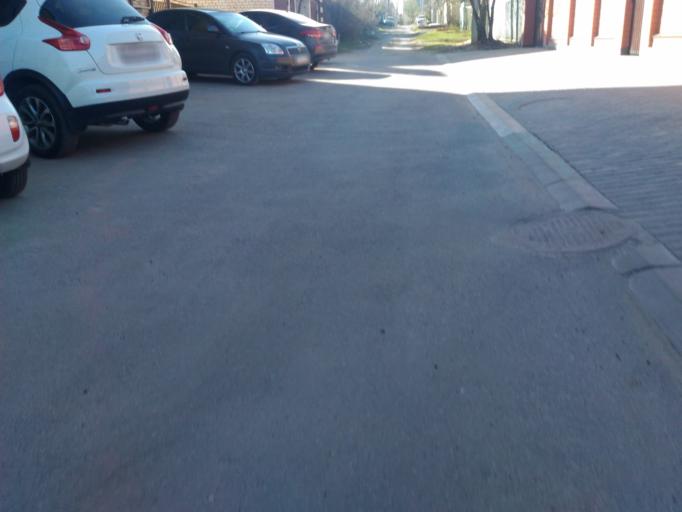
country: RU
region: Ulyanovsk
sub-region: Ulyanovskiy Rayon
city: Ulyanovsk
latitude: 54.3518
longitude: 48.3776
